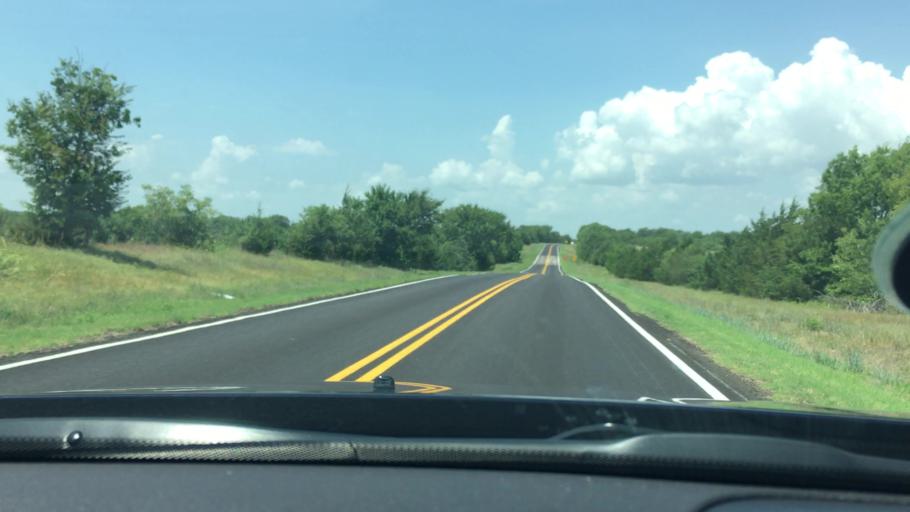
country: US
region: Oklahoma
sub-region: Marshall County
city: Kingston
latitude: 34.0887
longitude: -96.5948
